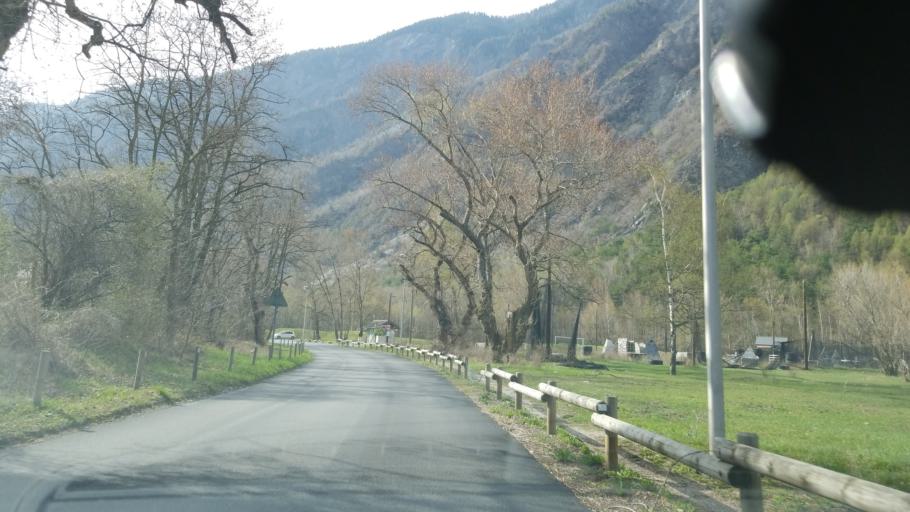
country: FR
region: Rhone-Alpes
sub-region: Departement de la Savoie
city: Villargondran
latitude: 45.2555
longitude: 6.3844
